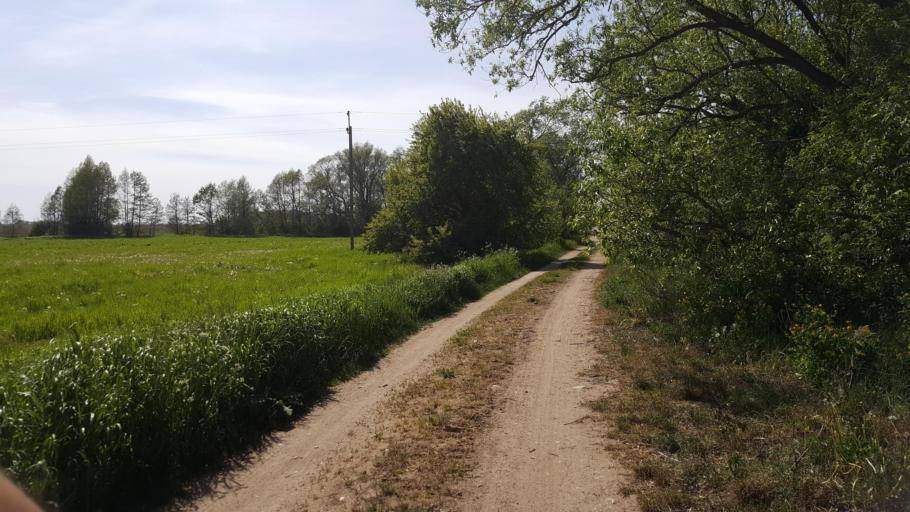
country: BY
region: Brest
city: Zhabinka
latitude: 52.3123
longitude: 24.0388
